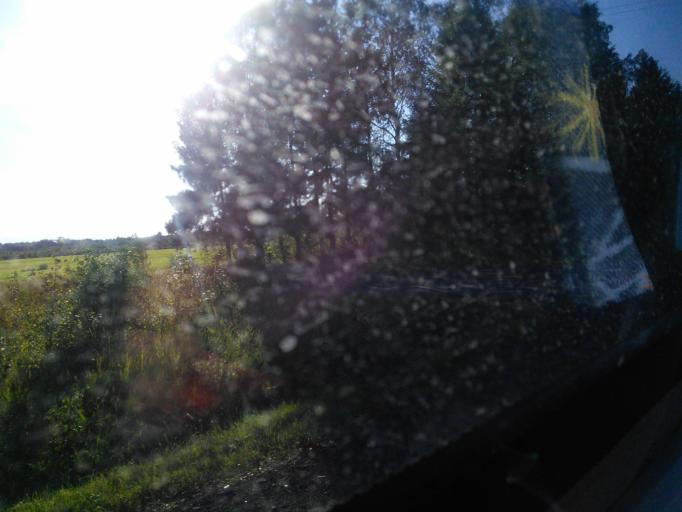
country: RU
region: Jaroslavl
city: Poshekhon'ye
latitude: 58.3648
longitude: 39.0293
